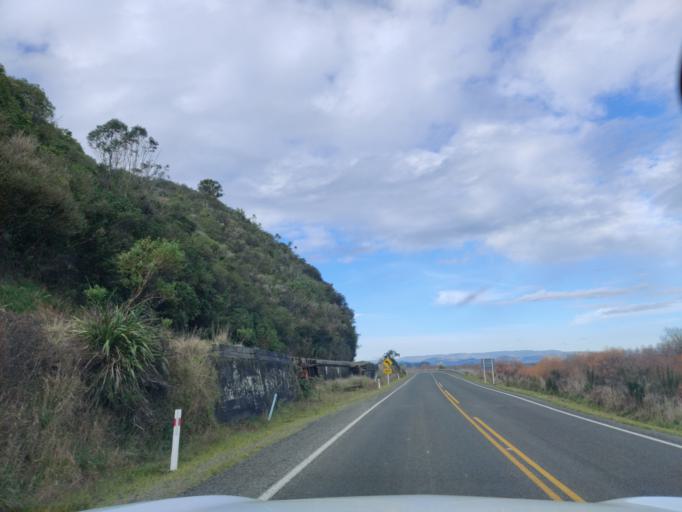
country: NZ
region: Manawatu-Wanganui
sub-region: Palmerston North City
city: Palmerston North
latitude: -40.3382
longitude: 175.8232
